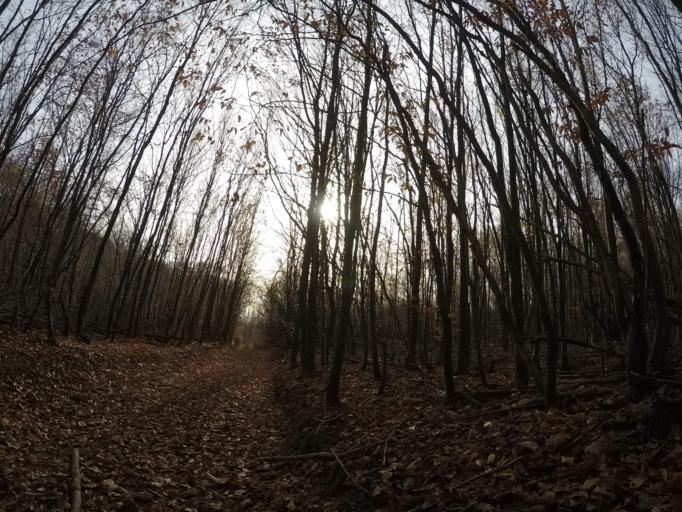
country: SK
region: Presovsky
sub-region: Okres Presov
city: Presov
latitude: 48.9168
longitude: 21.2121
